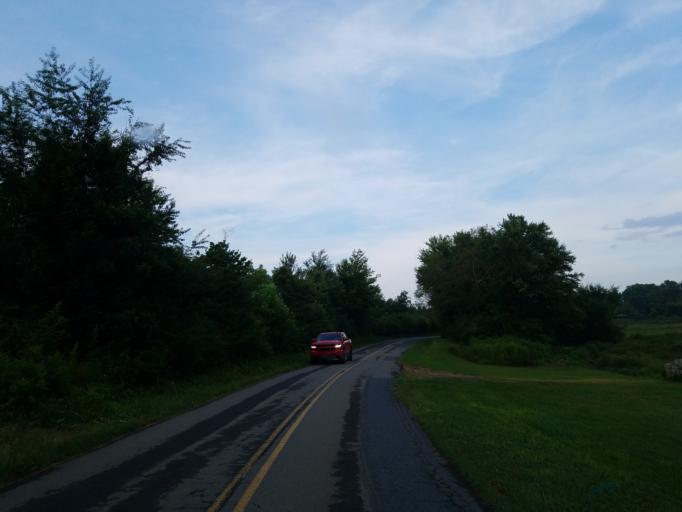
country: US
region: Georgia
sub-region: Pickens County
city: Jasper
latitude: 34.5059
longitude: -84.5256
